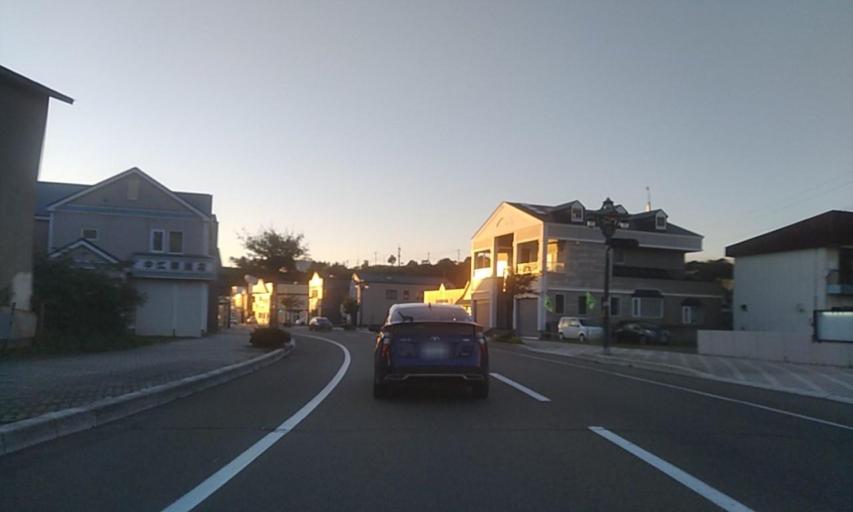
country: JP
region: Hokkaido
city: Shizunai-furukawacho
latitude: 42.1601
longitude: 142.7809
